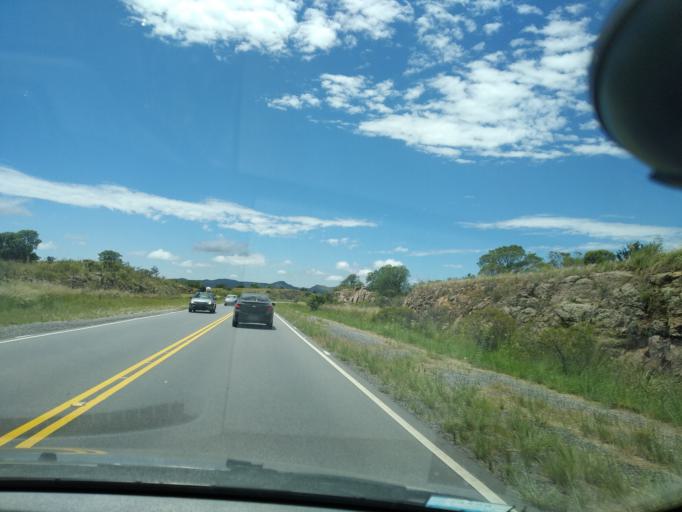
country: AR
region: Cordoba
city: Cuesta Blanca
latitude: -31.5835
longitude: -64.6270
